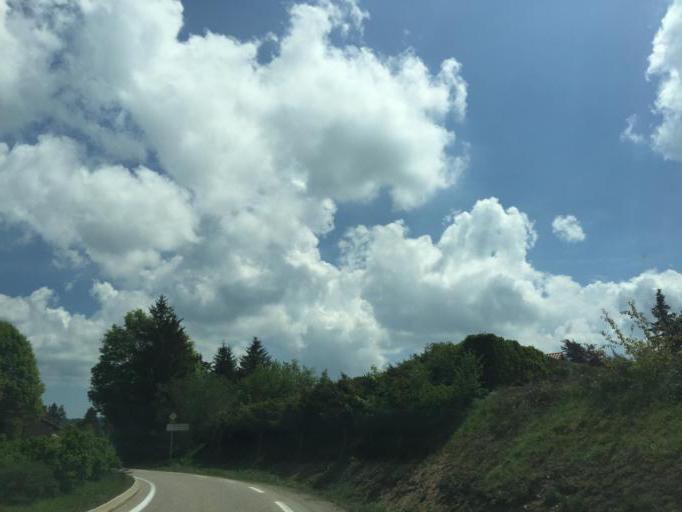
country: FR
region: Rhone-Alpes
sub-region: Departement de la Loire
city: Saint-Genest-Malifaux
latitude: 45.3609
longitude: 4.4575
